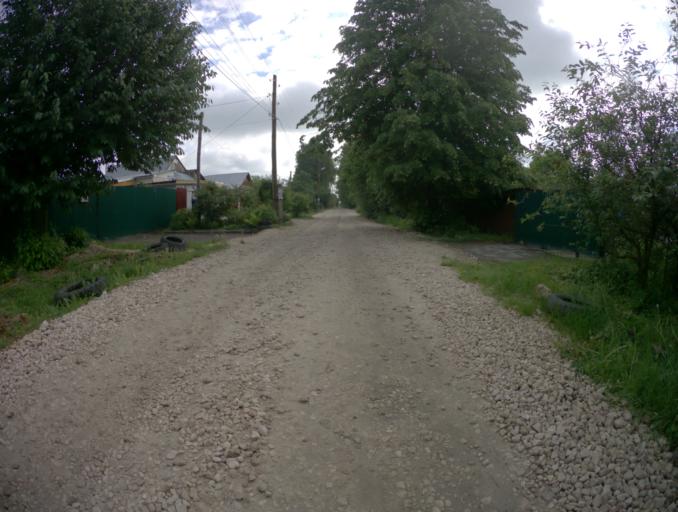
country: RU
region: Vladimir
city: Lakinsk
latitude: 56.0248
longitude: 39.9845
